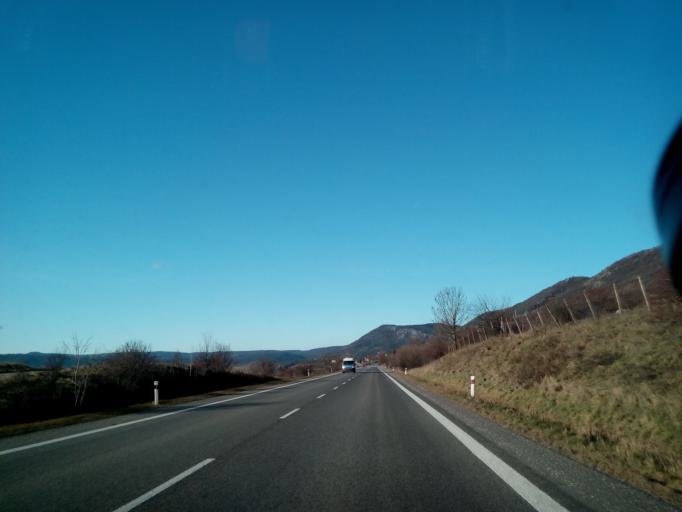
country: SK
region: Kosicky
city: Roznava
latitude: 48.5953
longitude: 20.6926
